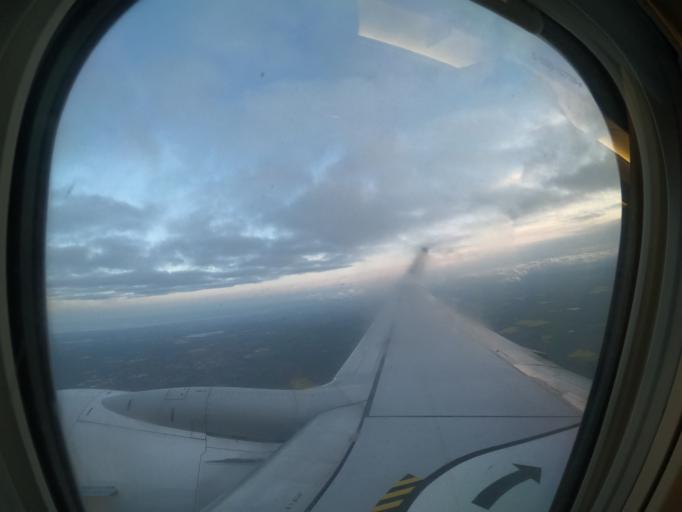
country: GB
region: England
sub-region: Essex
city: Chelmsford
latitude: 51.8213
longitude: 0.4407
